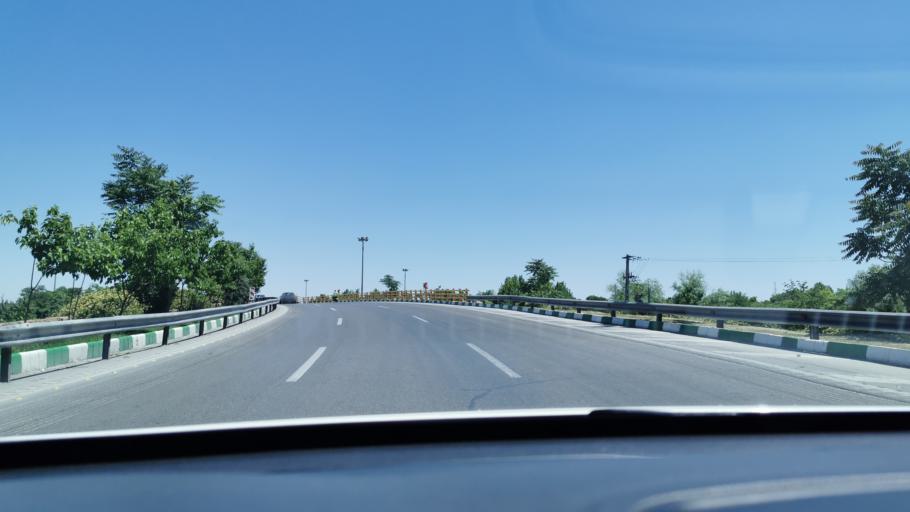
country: IR
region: Razavi Khorasan
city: Mashhad
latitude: 36.2499
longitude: 59.6082
